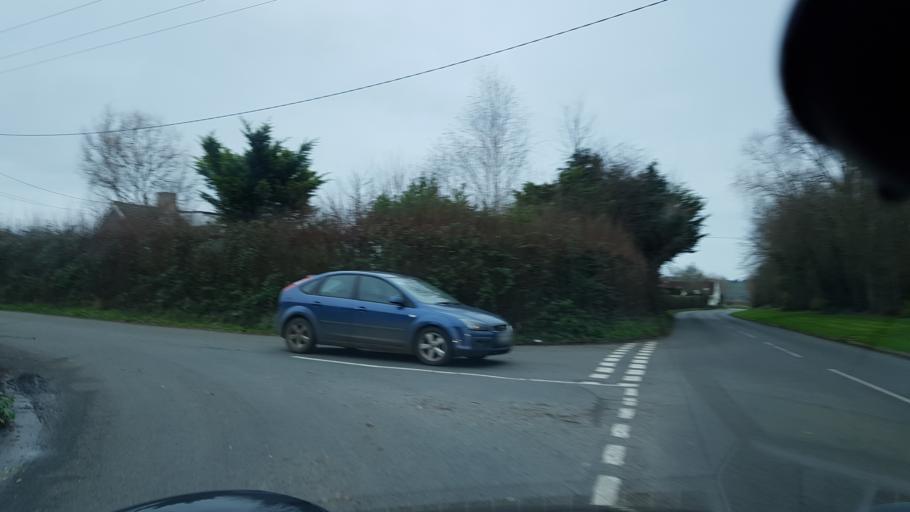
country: GB
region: England
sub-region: Somerset
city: Ilminster
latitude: 50.9510
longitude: -2.9073
